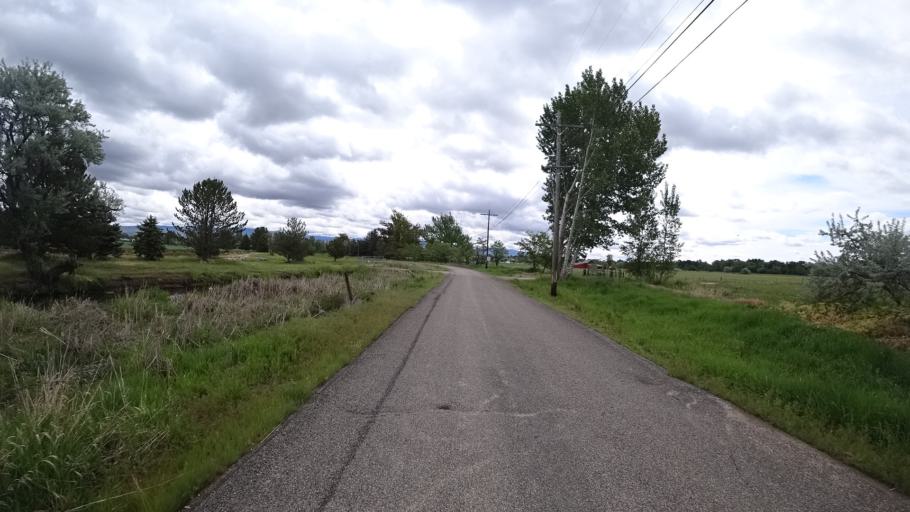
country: US
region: Idaho
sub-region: Ada County
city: Eagle
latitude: 43.6842
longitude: -116.3817
